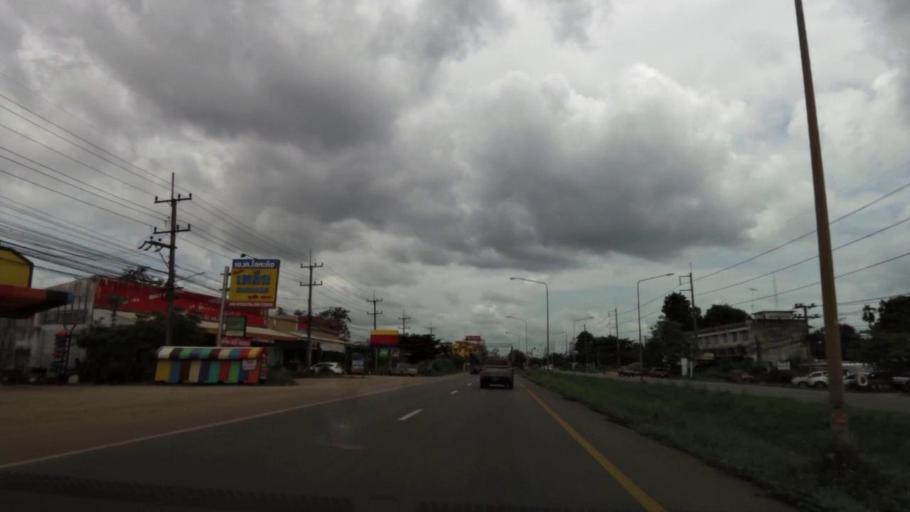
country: TH
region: Rayong
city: Klaeng
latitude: 12.7839
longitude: 101.6559
